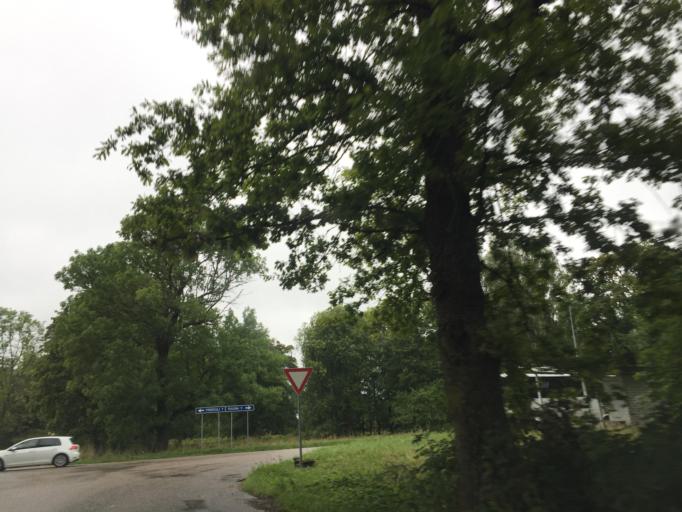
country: LV
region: Priekuli
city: Priekuli
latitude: 57.3285
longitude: 25.4702
